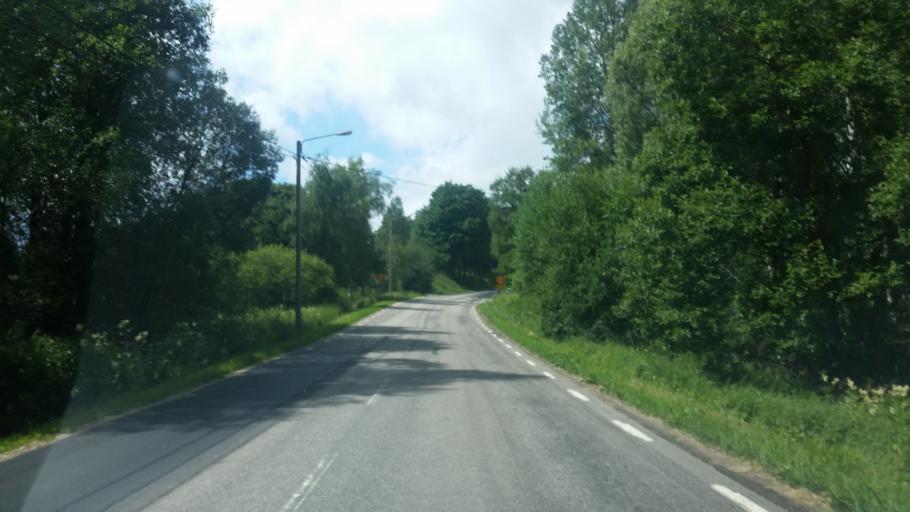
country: SE
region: Joenkoeping
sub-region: Gislaveds Kommun
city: Reftele
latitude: 57.1790
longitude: 13.5740
